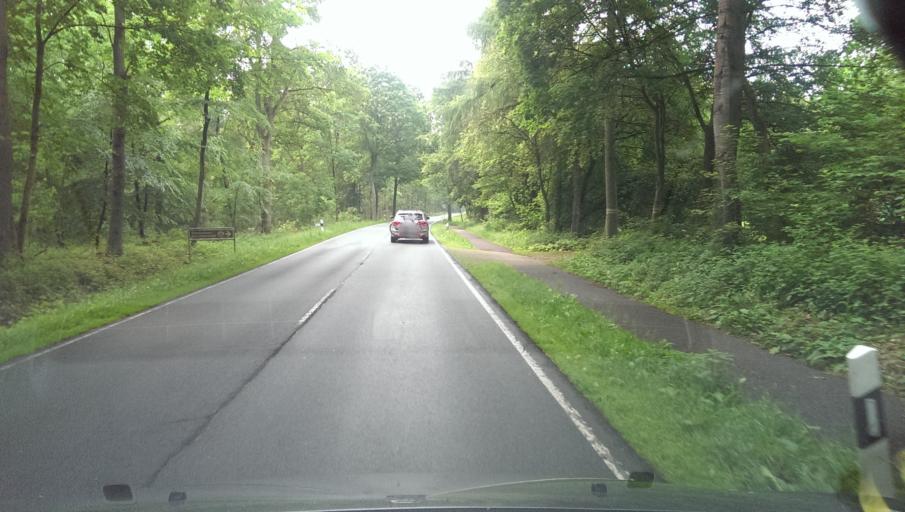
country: DE
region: Lower Saxony
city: Fassberg
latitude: 52.8749
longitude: 10.2065
